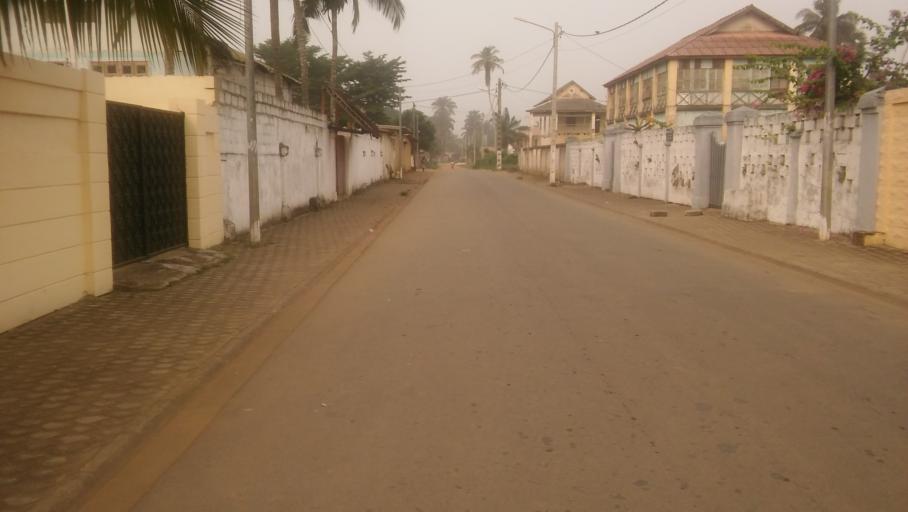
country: CI
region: Sud-Comoe
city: Grand-Bassam
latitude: 5.1971
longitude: -3.7382
